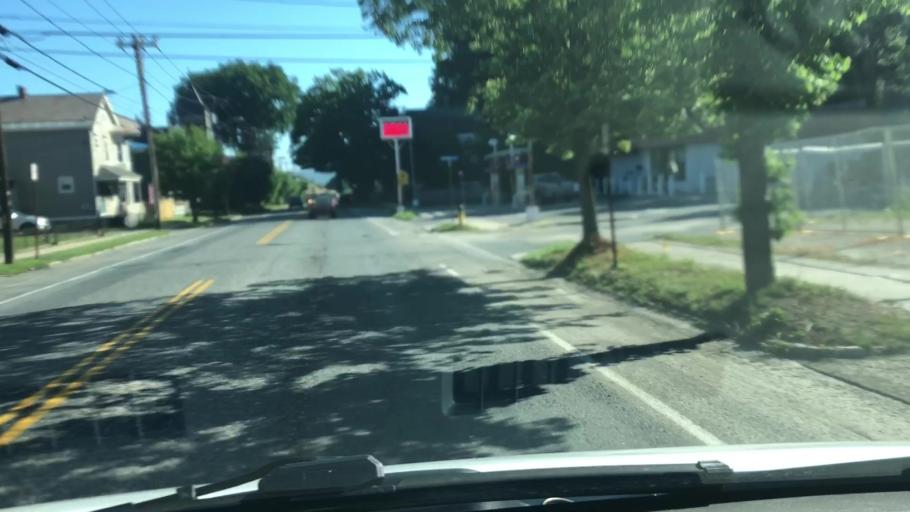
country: US
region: Massachusetts
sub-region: Berkshire County
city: Adams
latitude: 42.6165
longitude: -73.1226
